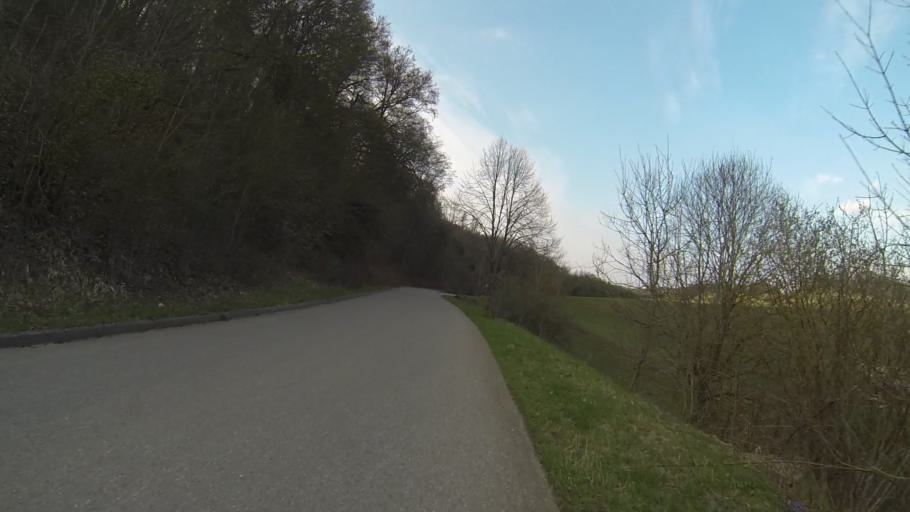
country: DE
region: Baden-Wuerttemberg
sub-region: Regierungsbezirk Stuttgart
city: Heidenheim an der Brenz
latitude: 48.6963
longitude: 10.1847
